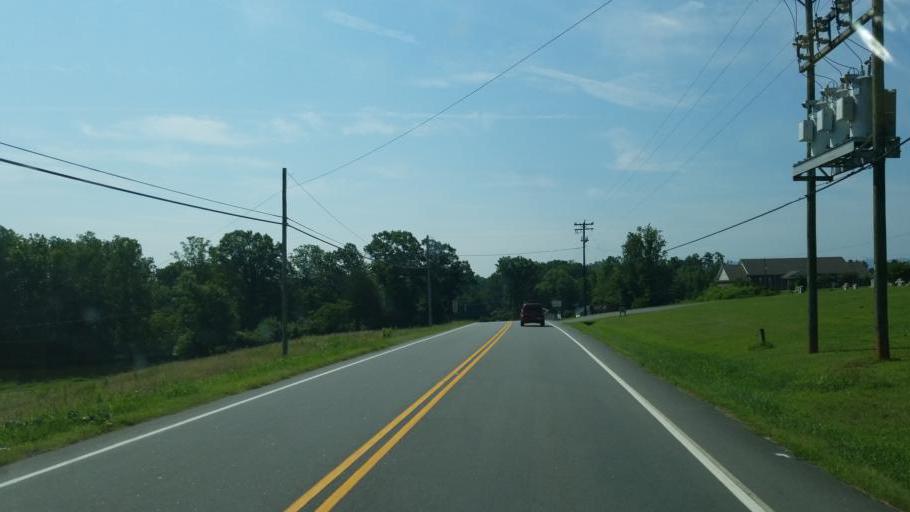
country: US
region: North Carolina
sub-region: Burke County
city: Glen Alpine
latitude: 35.7757
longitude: -81.7544
